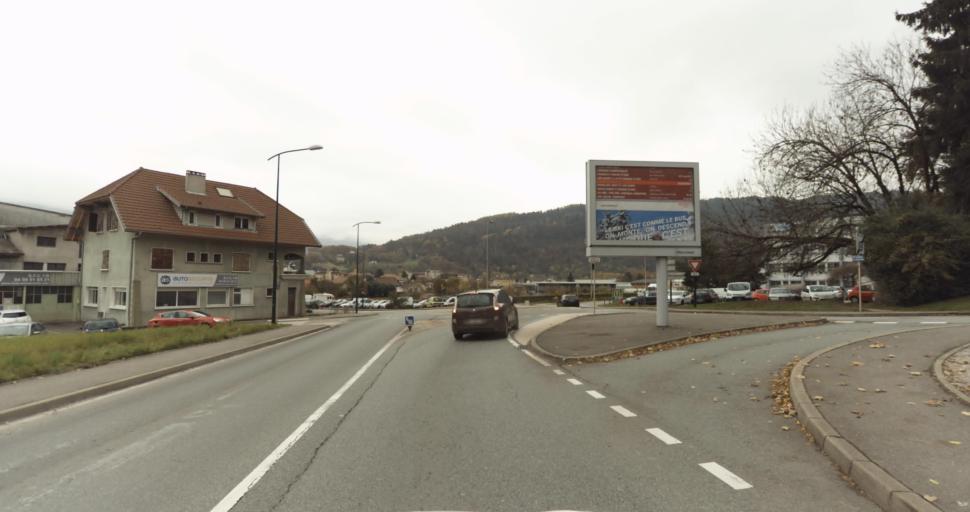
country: FR
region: Rhone-Alpes
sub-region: Departement de la Haute-Savoie
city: Annecy
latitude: 45.8949
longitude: 6.1129
